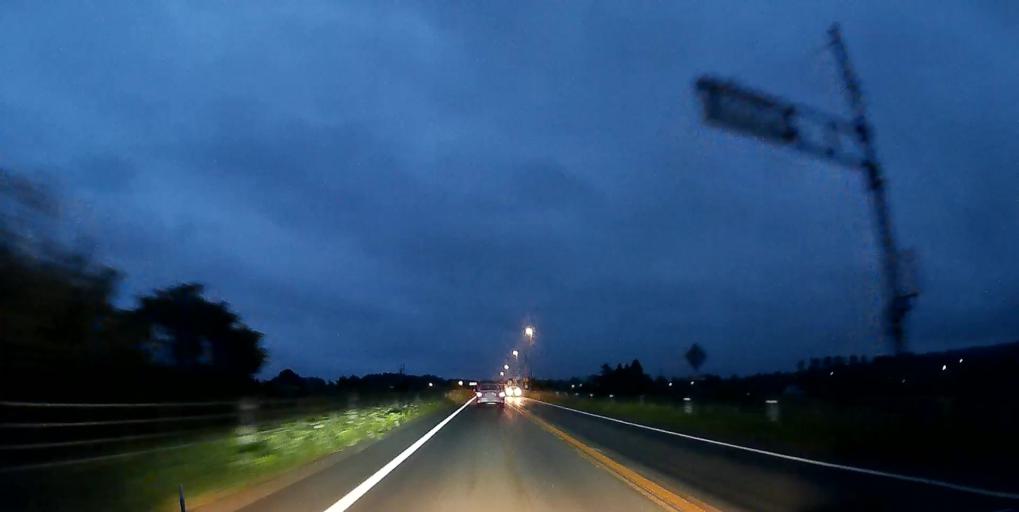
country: JP
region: Hokkaido
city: Nanae
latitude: 42.2109
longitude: 140.3938
